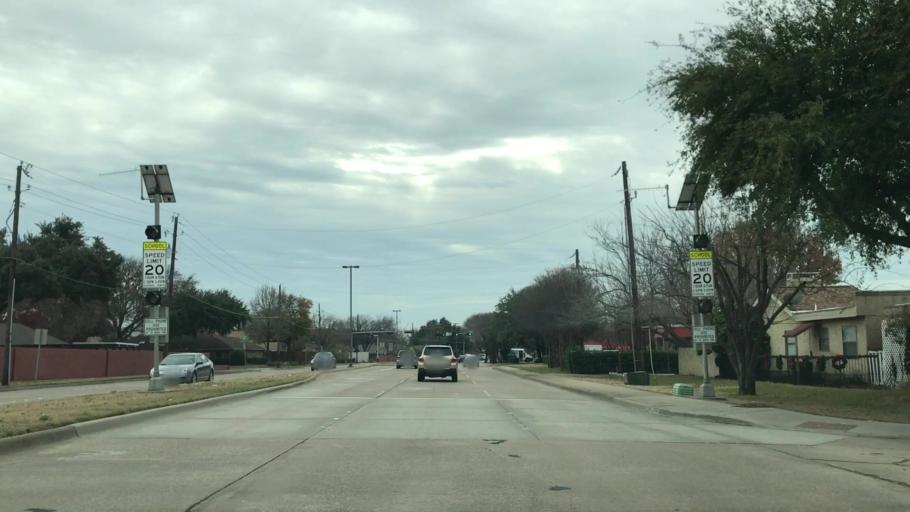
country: US
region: Texas
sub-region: Denton County
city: The Colony
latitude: 33.0213
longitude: -96.8850
